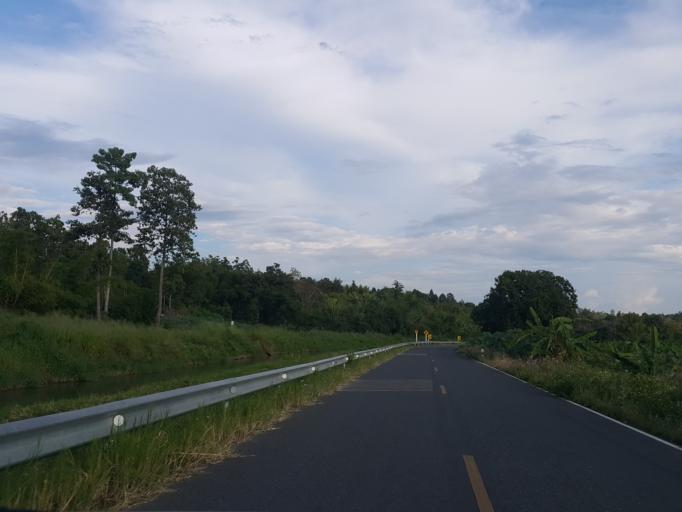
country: TH
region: Chiang Mai
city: San Sai
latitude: 18.9672
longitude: 98.9899
